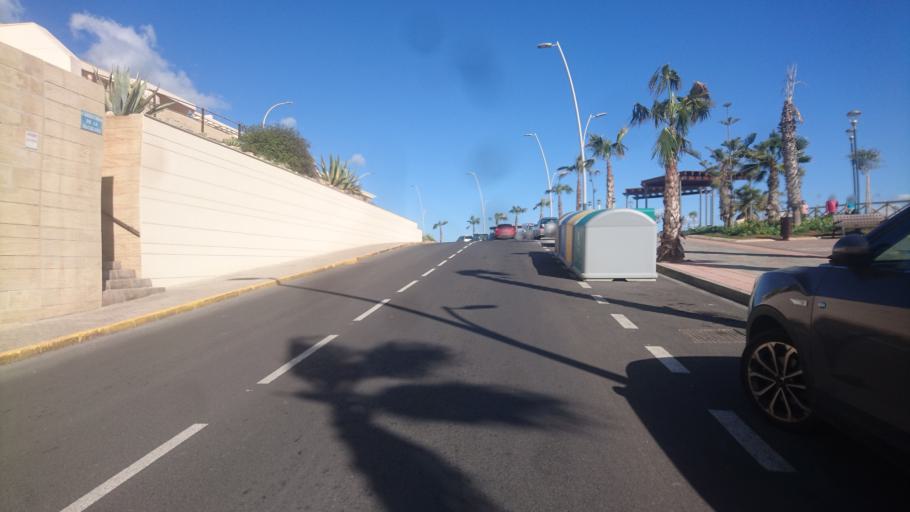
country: ES
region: Melilla
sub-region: Melilla
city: Melilla
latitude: 35.2951
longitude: -2.9362
